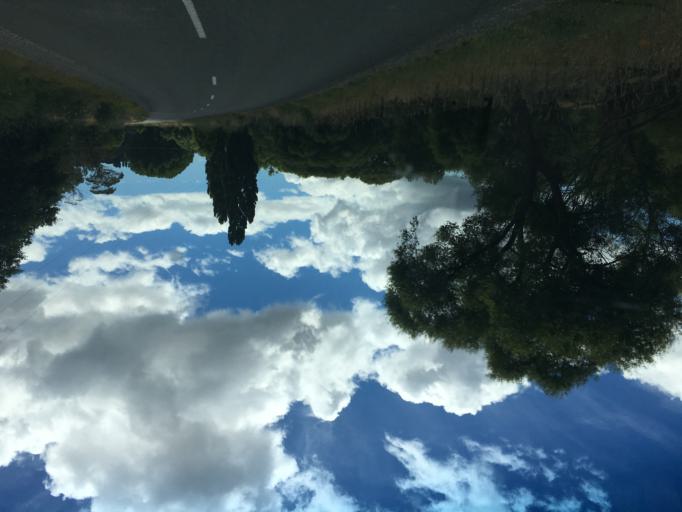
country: NZ
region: Hawke's Bay
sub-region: Hastings District
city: Hastings
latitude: -39.7495
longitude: 176.8776
